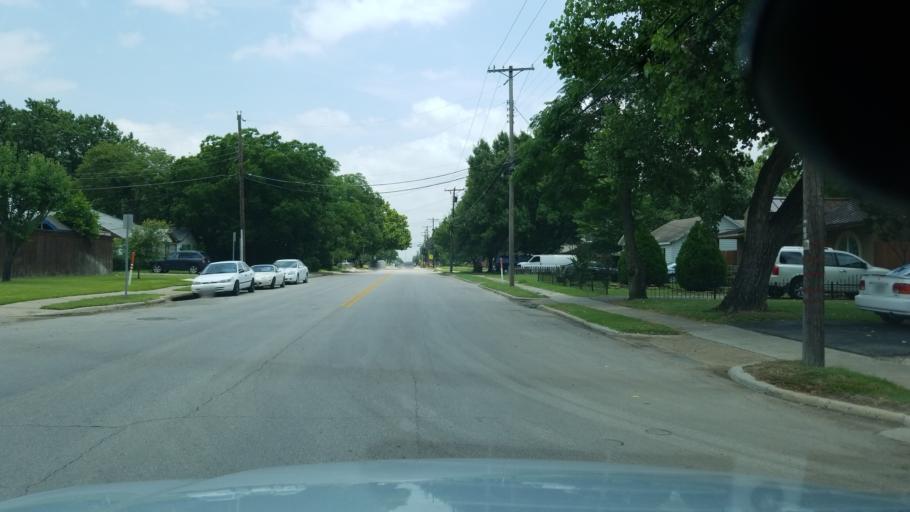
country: US
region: Texas
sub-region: Dallas County
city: Irving
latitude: 32.8176
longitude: -96.9321
